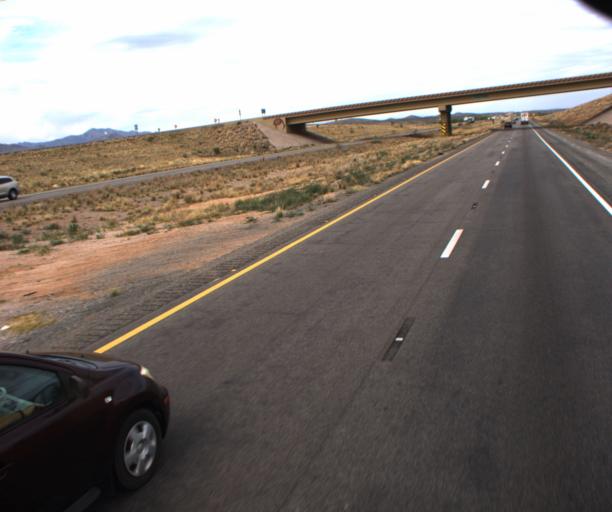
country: US
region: Arizona
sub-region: Cochise County
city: Mescal
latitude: 31.9817
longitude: -110.5346
